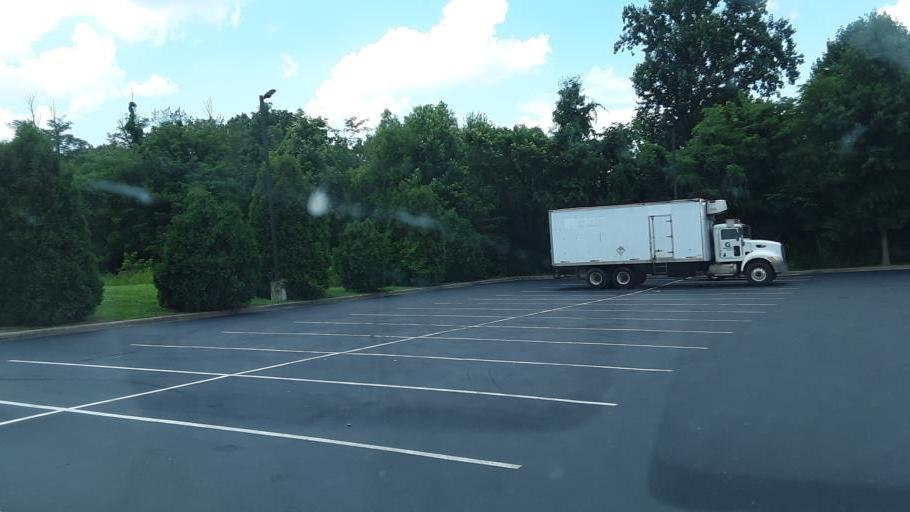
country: US
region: Tennessee
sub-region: Montgomery County
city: Clarksville
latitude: 36.5961
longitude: -87.2905
